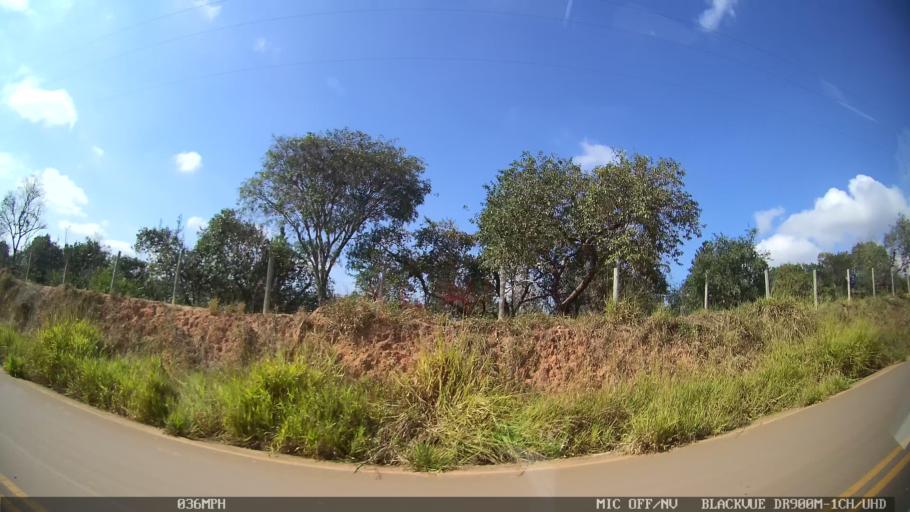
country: BR
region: Sao Paulo
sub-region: Indaiatuba
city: Indaiatuba
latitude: -22.9968
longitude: -47.1992
